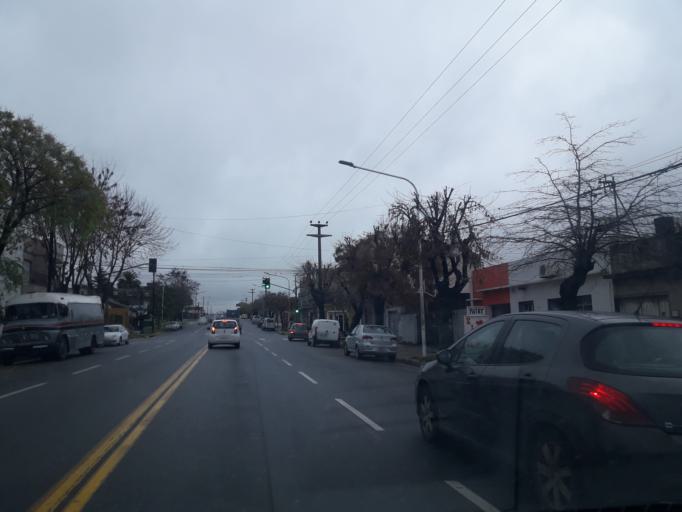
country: AR
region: Buenos Aires
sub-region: Partido de Tandil
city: Tandil
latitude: -37.3193
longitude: -59.1511
